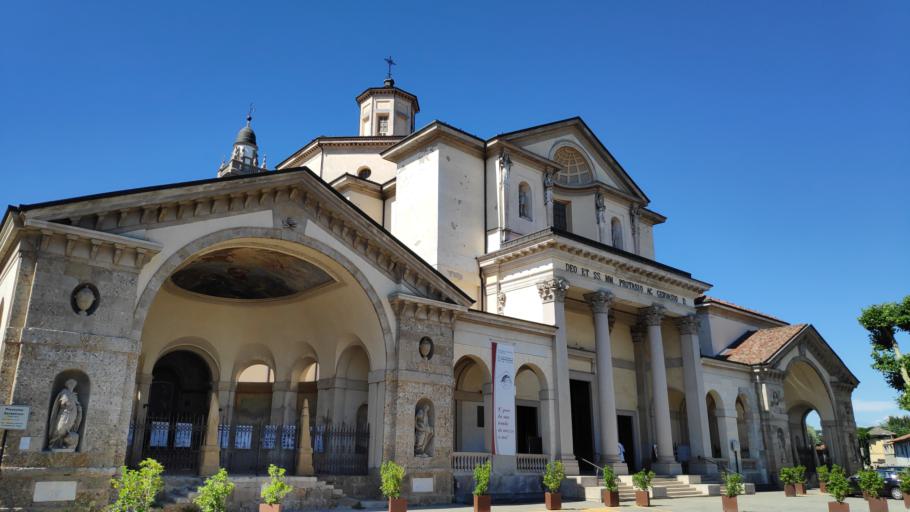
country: IT
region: Lombardy
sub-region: Citta metropolitana di Milano
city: Gorgonzola
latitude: 45.5308
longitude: 9.4082
